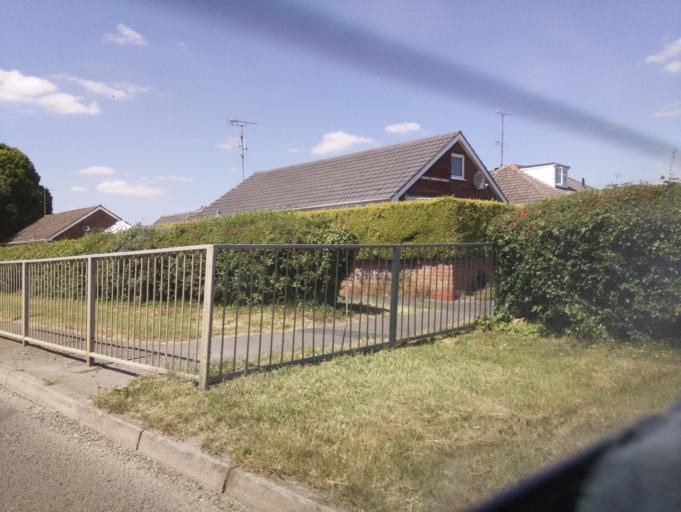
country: GB
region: England
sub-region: Borough of Swindon
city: Wroughton
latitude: 51.5289
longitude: -1.8028
